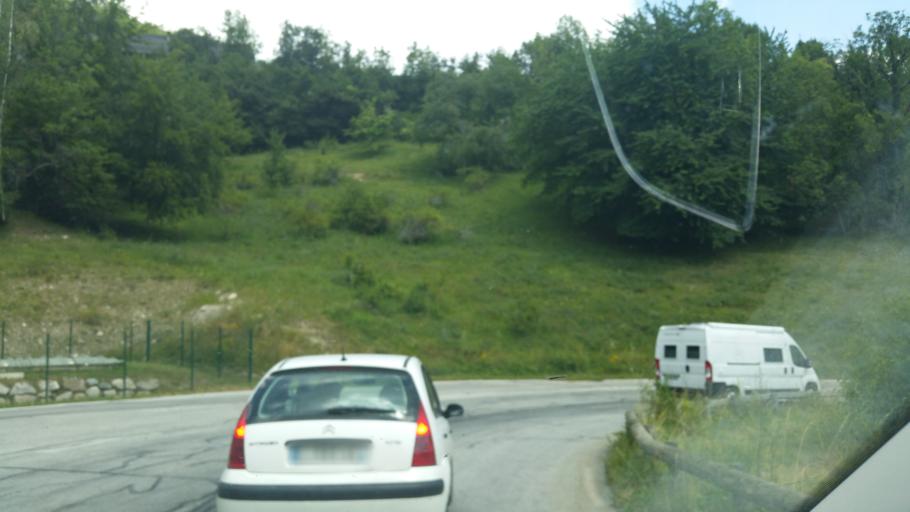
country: FR
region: Rhone-Alpes
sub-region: Departement de la Savoie
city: Saint-Jean-de-Maurienne
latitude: 45.2505
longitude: 6.3159
